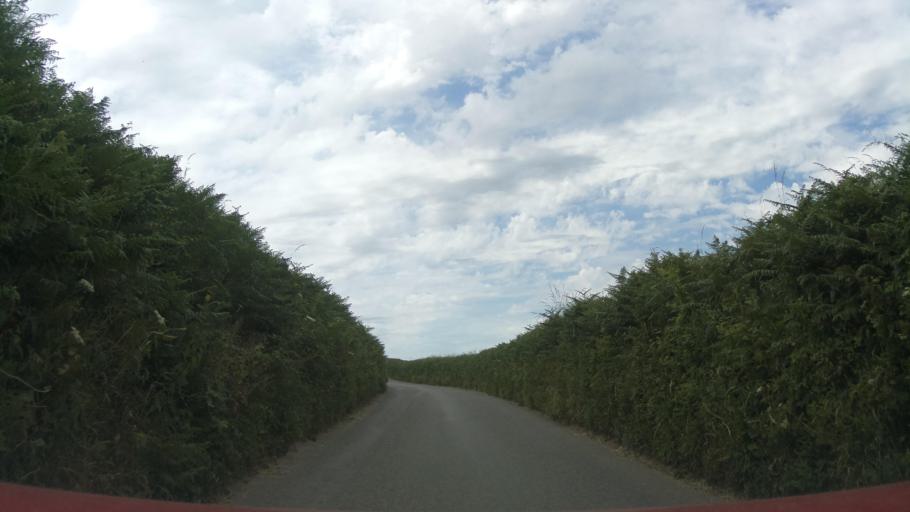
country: GB
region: England
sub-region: Devon
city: Dartmouth
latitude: 50.3607
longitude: -3.6397
